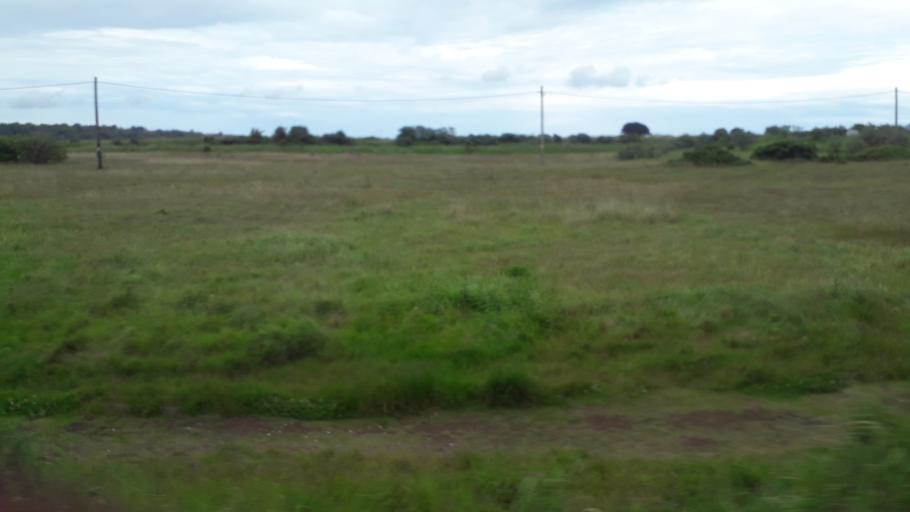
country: IE
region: Leinster
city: Dollymount
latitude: 53.3572
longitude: -6.1749
